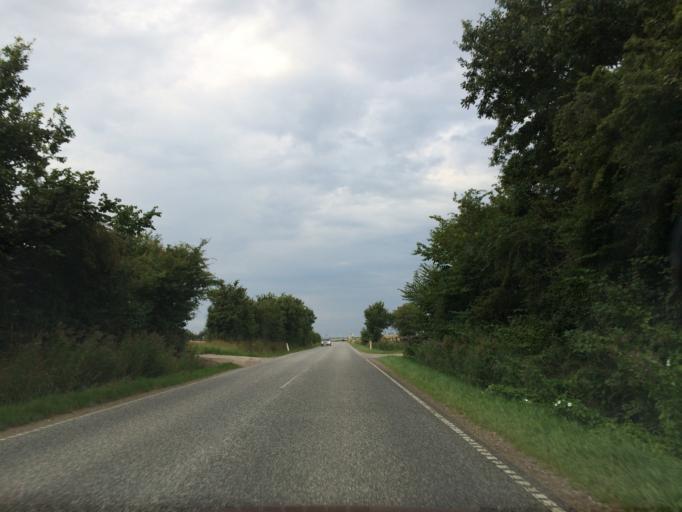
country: DK
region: South Denmark
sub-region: Sonderborg Kommune
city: Broager
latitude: 54.9303
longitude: 9.6896
